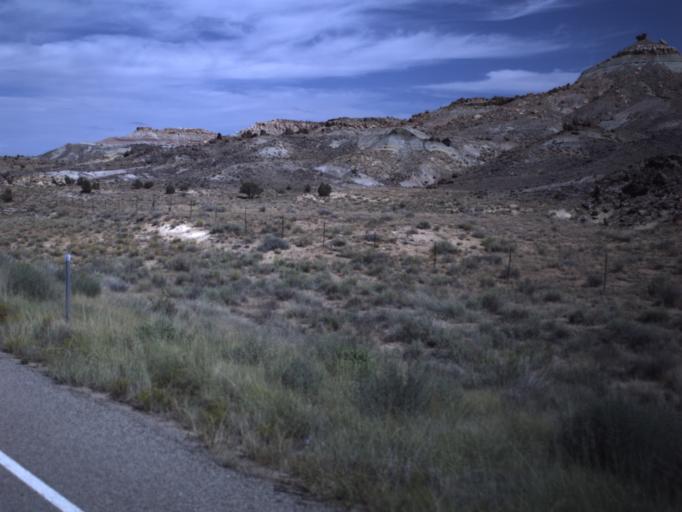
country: US
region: Colorado
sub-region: Montezuma County
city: Towaoc
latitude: 37.1801
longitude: -109.1248
